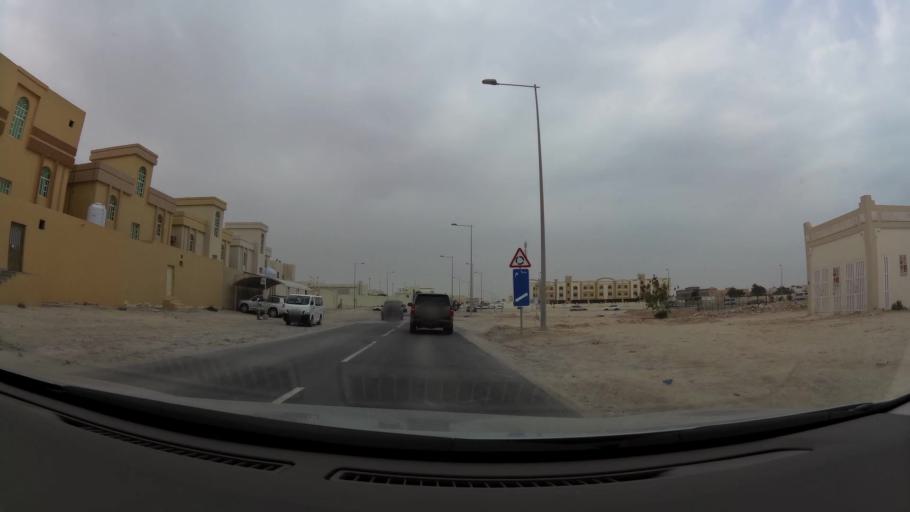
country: QA
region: Baladiyat ar Rayyan
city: Ar Rayyan
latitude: 25.3413
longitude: 51.4711
